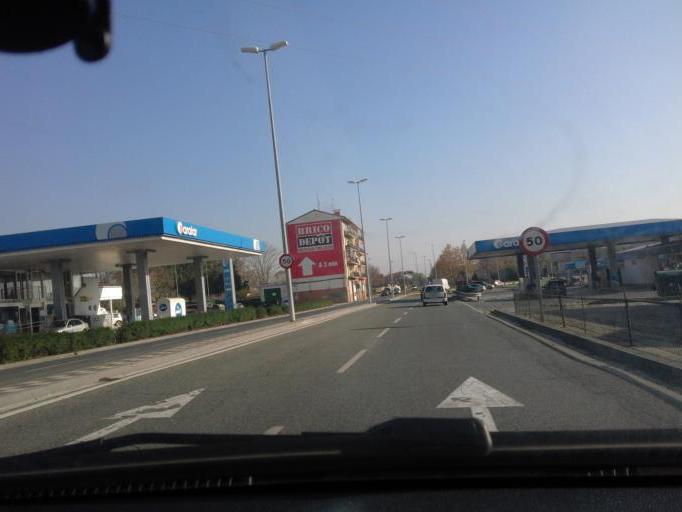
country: ES
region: Navarre
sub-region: Provincia de Navarra
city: Berriobeiti
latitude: 42.8435
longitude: -1.6823
